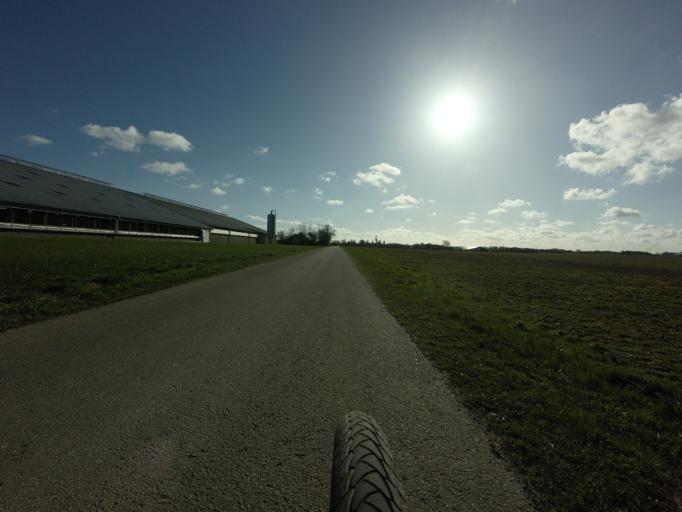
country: DK
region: North Denmark
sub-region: Hjorring Kommune
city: Vra
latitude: 57.3618
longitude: 9.8329
